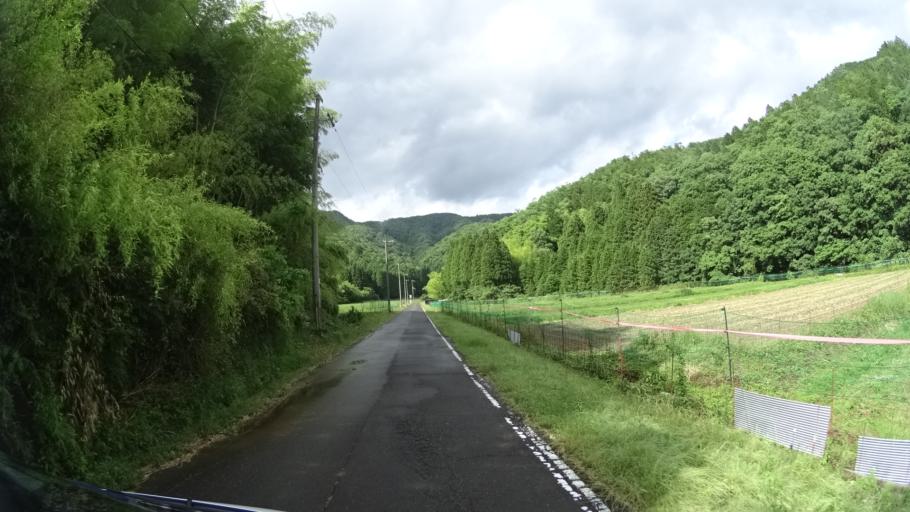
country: JP
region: Kyoto
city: Ayabe
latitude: 35.3899
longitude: 135.2589
